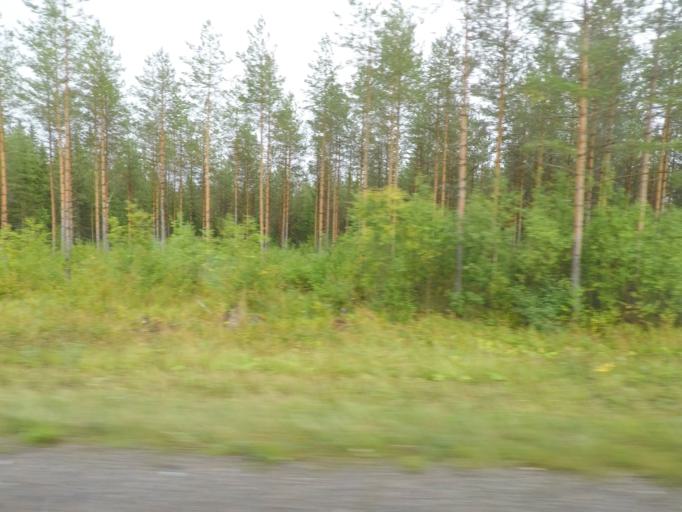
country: FI
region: Southern Savonia
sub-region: Pieksaemaeki
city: Joroinen
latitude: 62.0881
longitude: 27.8247
